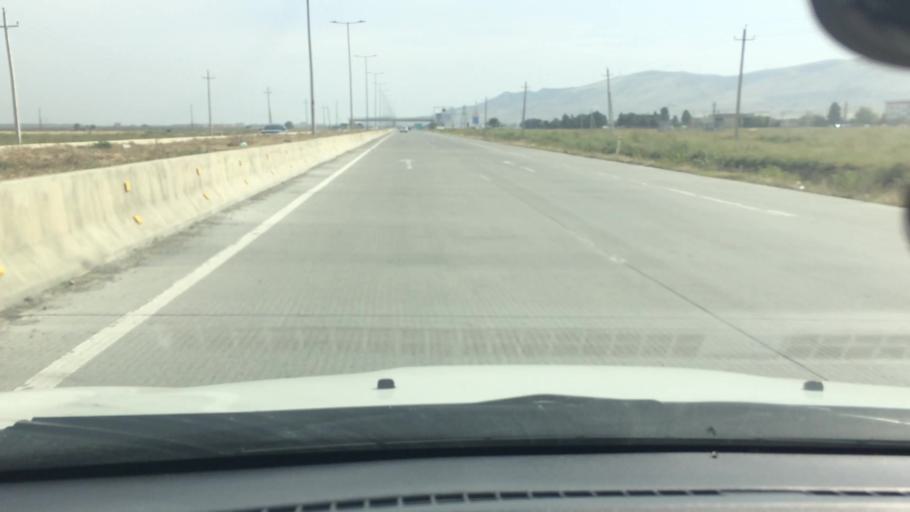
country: GE
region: Kvemo Kartli
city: Rust'avi
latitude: 41.5977
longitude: 44.9424
